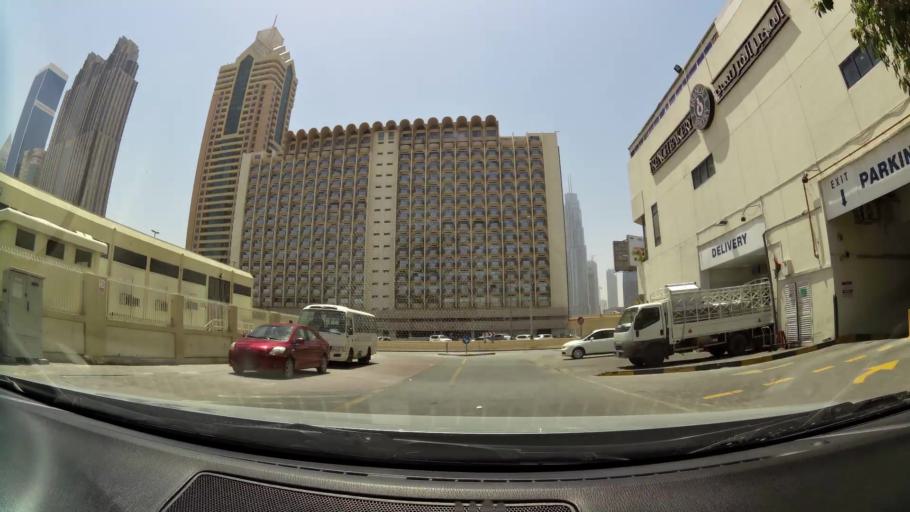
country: AE
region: Dubai
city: Dubai
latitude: 25.2068
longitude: 55.2690
